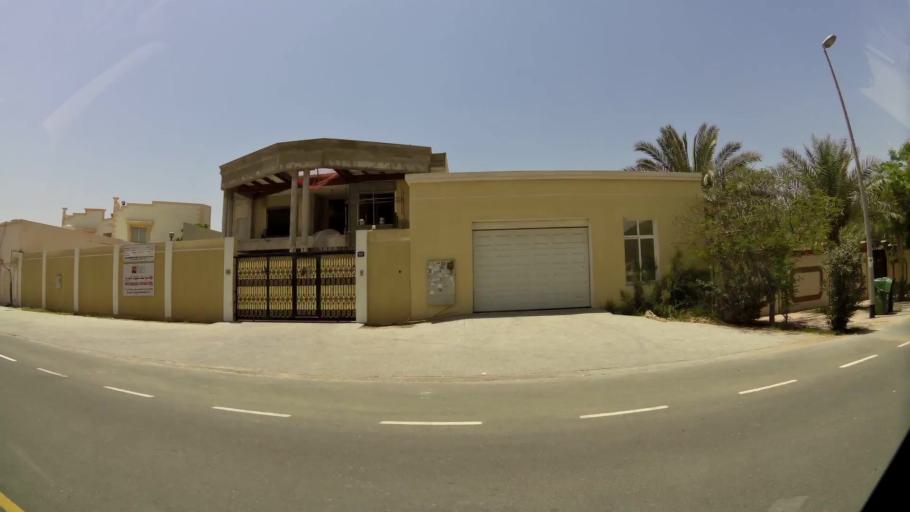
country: AE
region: Dubai
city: Dubai
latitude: 25.0827
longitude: 55.2089
